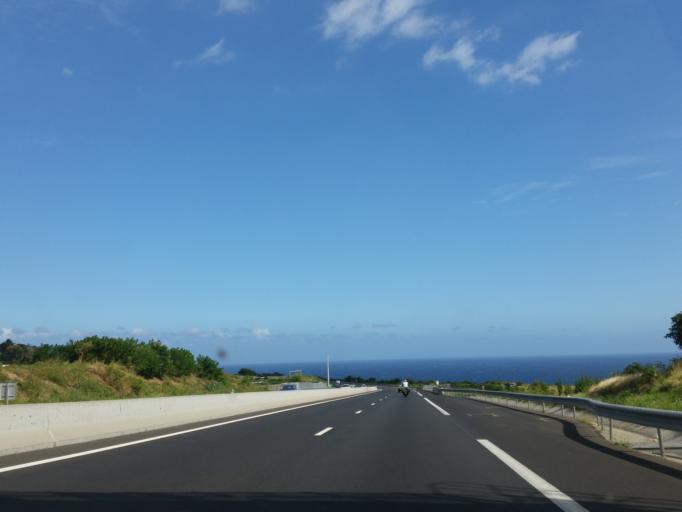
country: RE
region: Reunion
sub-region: Reunion
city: Saint-Leu
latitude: -21.1987
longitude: 55.2947
